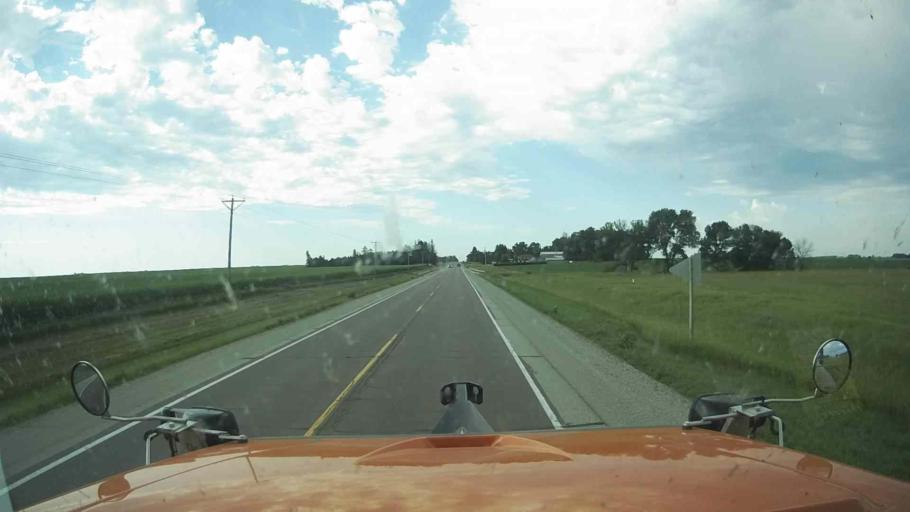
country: US
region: Iowa
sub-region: Cerro Gordo County
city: Mason City
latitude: 43.0751
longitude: -93.2014
